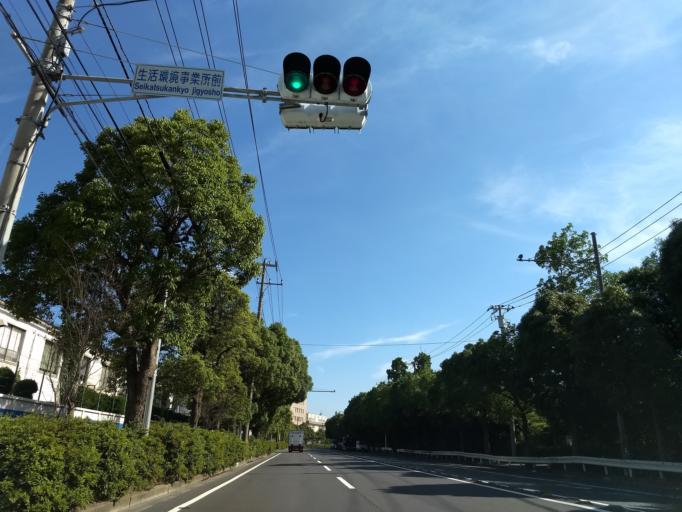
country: JP
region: Kanagawa
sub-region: Kawasaki-shi
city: Kawasaki
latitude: 35.5302
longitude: 139.7495
